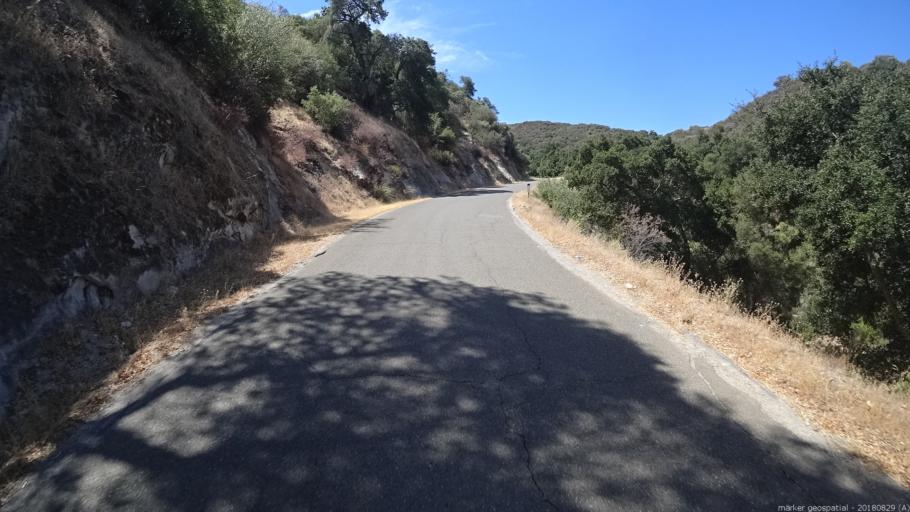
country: US
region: California
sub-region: San Luis Obispo County
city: Lake Nacimiento
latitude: 35.8331
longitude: -121.0490
